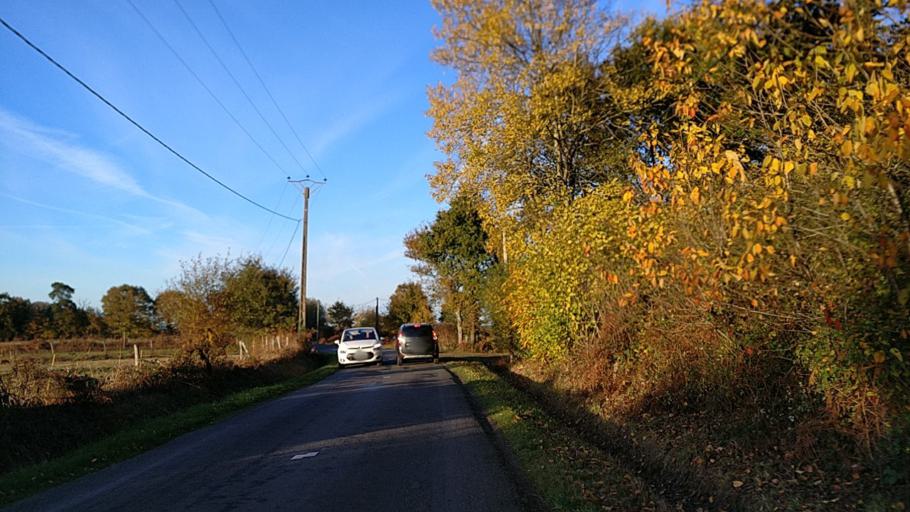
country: FR
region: Brittany
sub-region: Departement d'Ille-et-Vilaine
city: Saint-Sulpice-la-Foret
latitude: 48.2016
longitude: -1.5767
